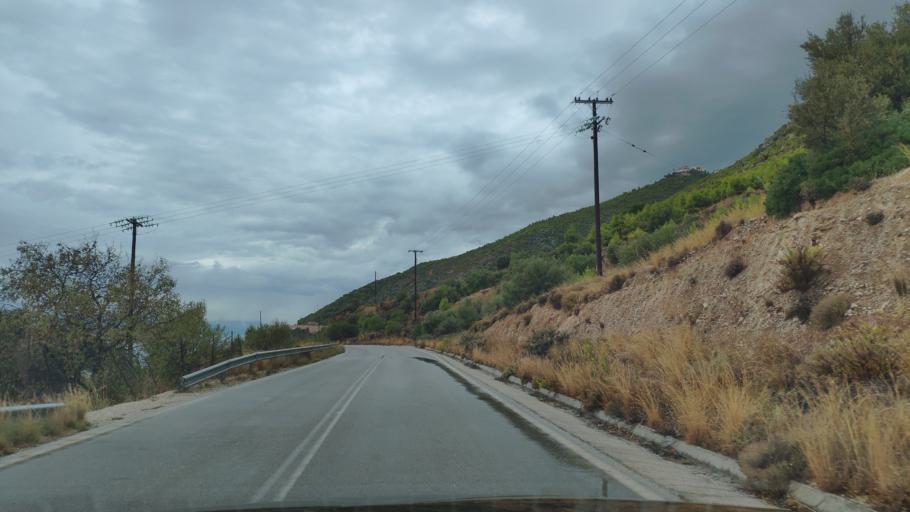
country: GR
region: Peloponnese
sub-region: Nomos Korinthias
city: Loutraki
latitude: 37.9804
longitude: 22.9822
